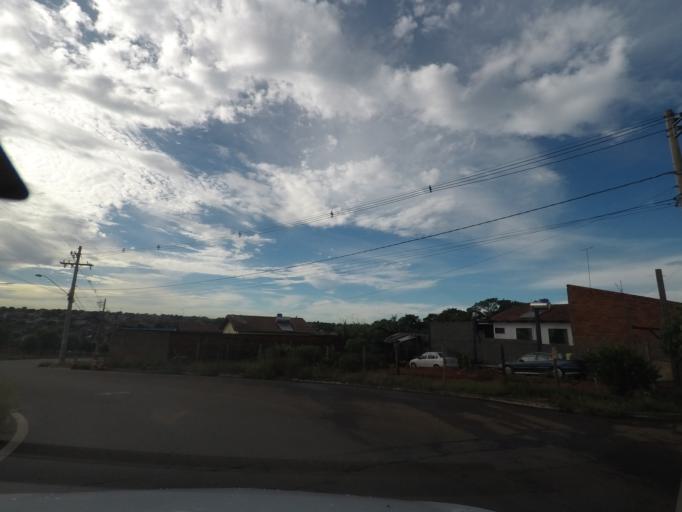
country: BR
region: Goias
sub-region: Aparecida De Goiania
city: Aparecida de Goiania
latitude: -16.7844
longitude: -49.3814
